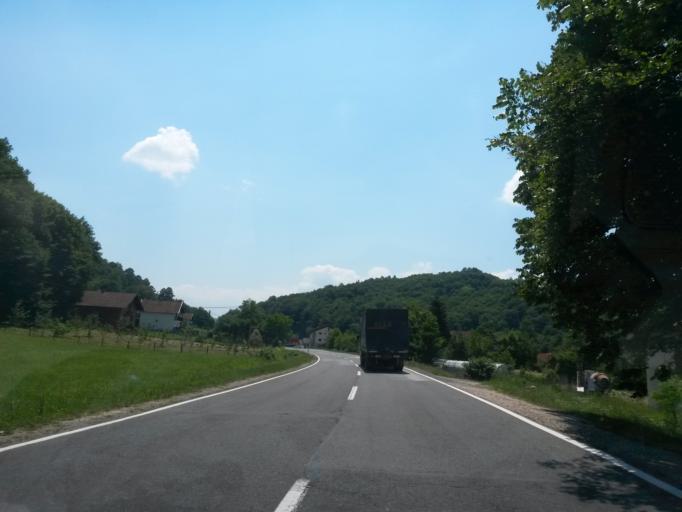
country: BA
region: Federation of Bosnia and Herzegovina
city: Lijesnica
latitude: 44.5038
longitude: 18.0795
